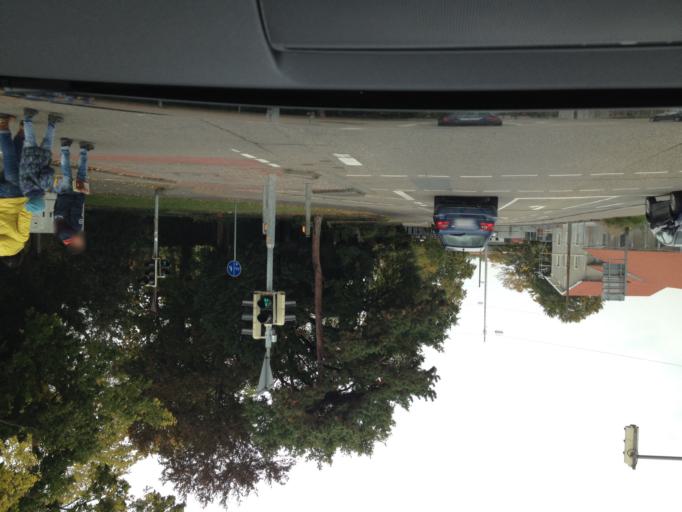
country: DE
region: Rheinland-Pfalz
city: Speyer
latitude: 49.3223
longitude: 8.4294
